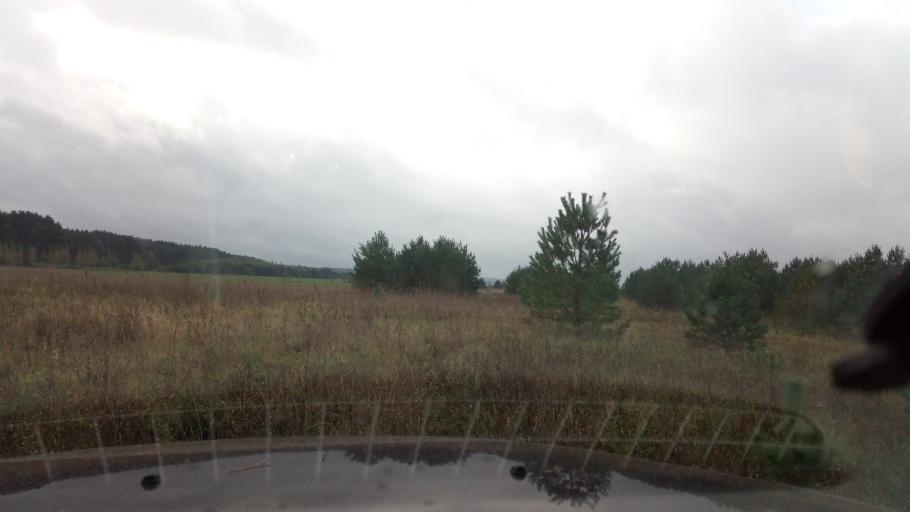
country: LT
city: Skaidiskes
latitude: 54.6219
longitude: 25.5214
